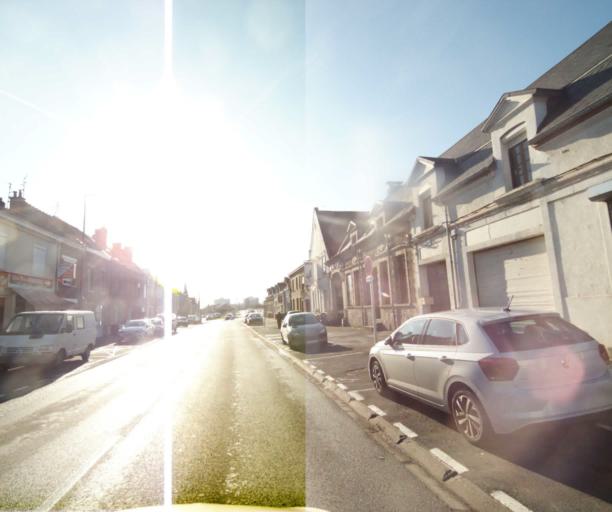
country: FR
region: Nord-Pas-de-Calais
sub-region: Departement du Nord
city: Aulnoy-lez-Valenciennes
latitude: 50.3401
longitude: 3.5251
